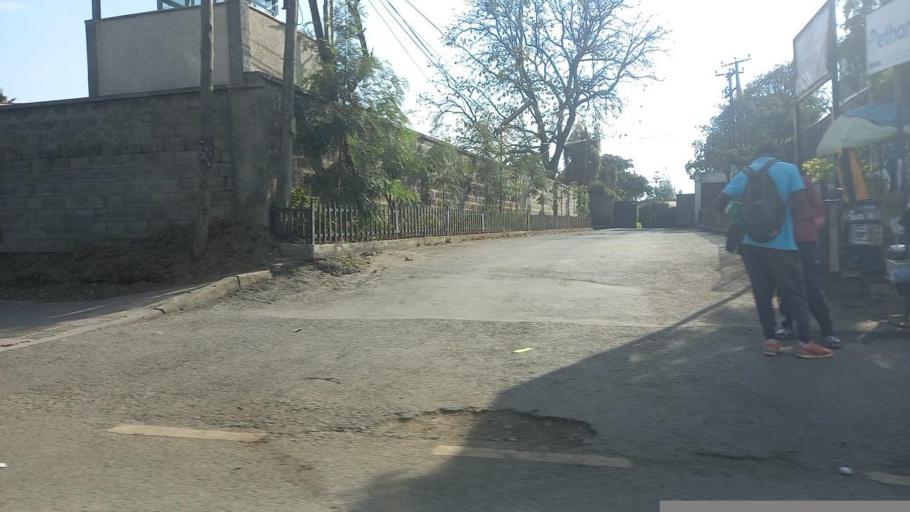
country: ET
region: Adis Abeba
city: Addis Ababa
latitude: 8.9964
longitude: 38.7352
